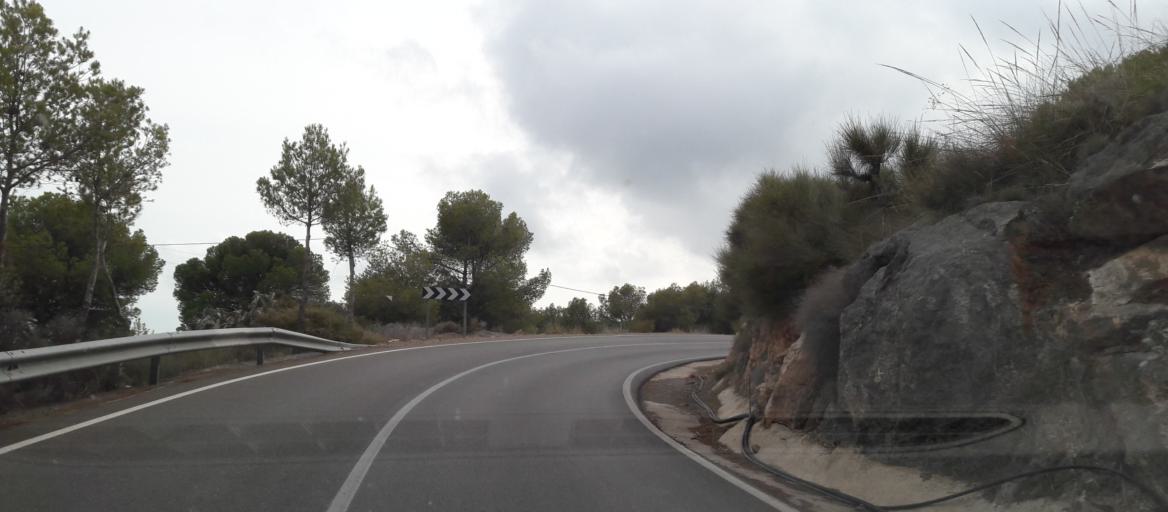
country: ES
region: Andalusia
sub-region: Provincia de Almeria
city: Enix
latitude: 36.8757
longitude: -2.6081
